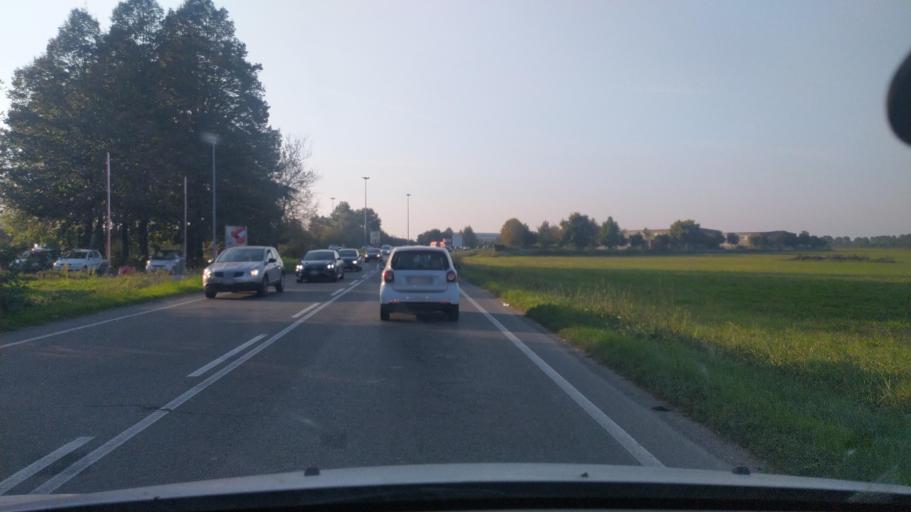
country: IT
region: Lombardy
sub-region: Provincia di Cremona
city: Capergnanica
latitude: 45.3613
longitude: 9.6391
